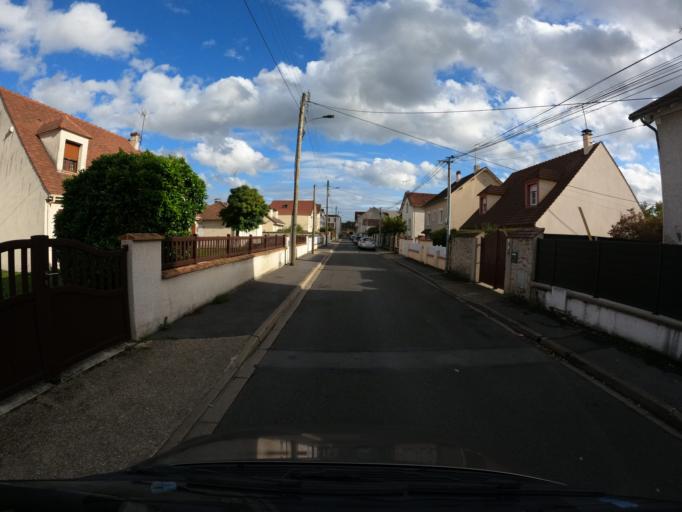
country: FR
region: Ile-de-France
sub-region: Departement de Seine-et-Marne
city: Esbly
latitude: 48.9015
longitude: 2.8092
